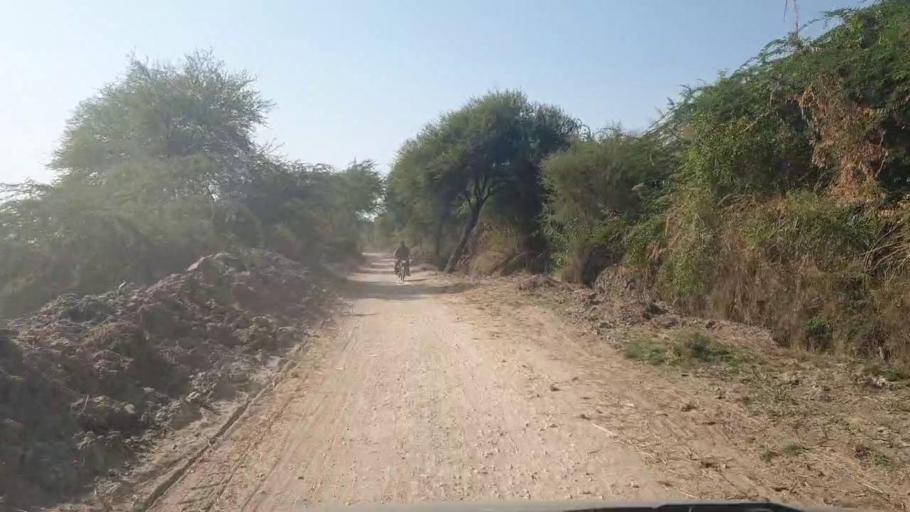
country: PK
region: Sindh
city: Badin
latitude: 24.5799
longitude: 68.7962
